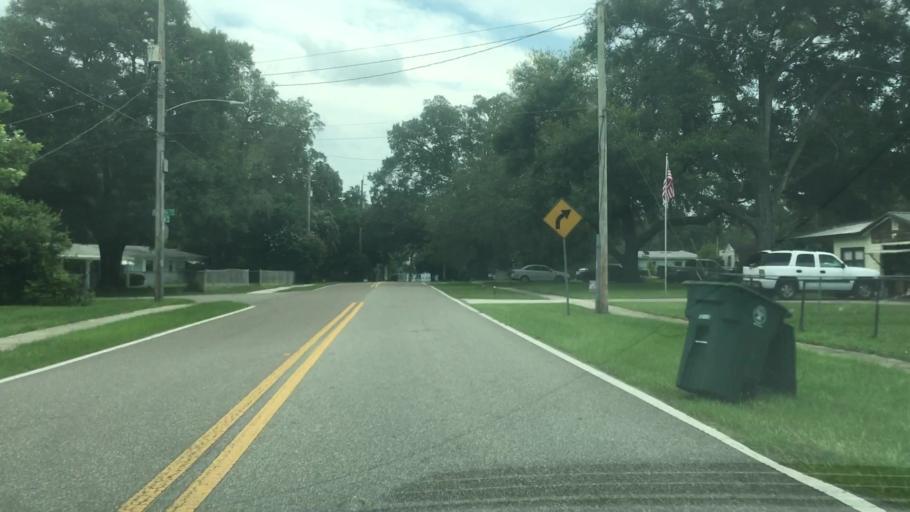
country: US
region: Florida
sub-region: Duval County
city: Jacksonville
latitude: 30.2941
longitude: -81.5495
